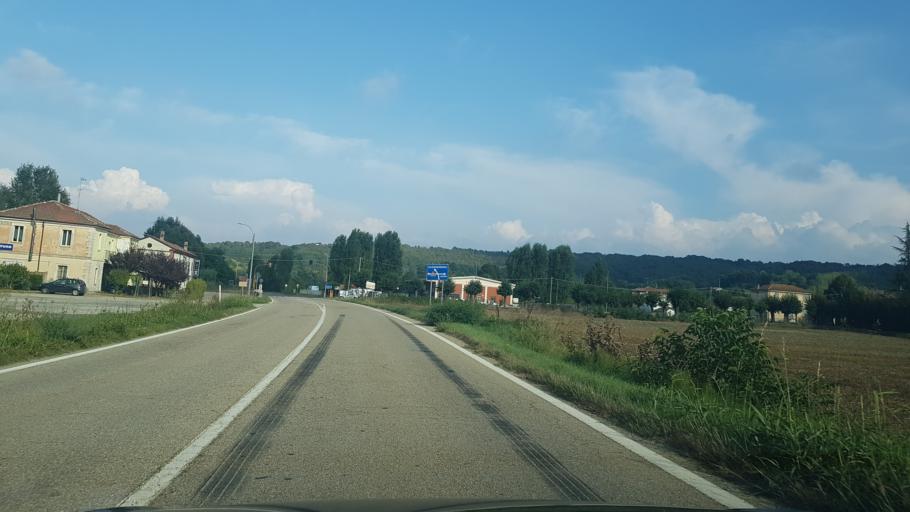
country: IT
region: Piedmont
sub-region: Provincia di Asti
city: Bruno
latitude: 44.7976
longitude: 8.4379
